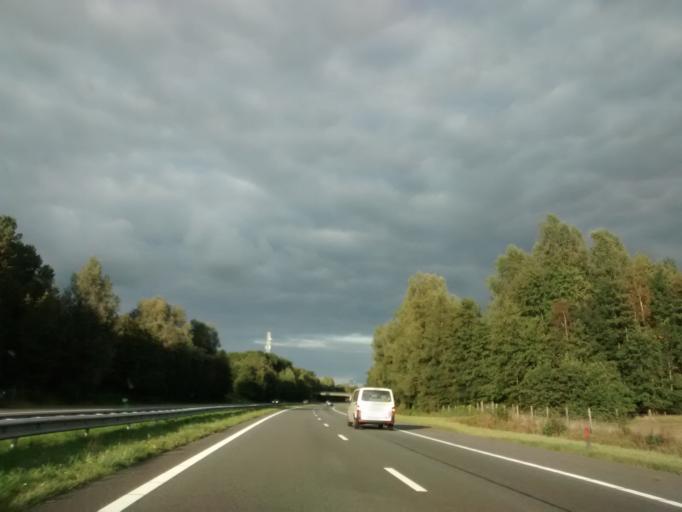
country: NL
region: Overijssel
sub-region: Gemeente Oldenzaal
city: Oldenzaal
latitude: 52.3031
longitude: 6.9737
